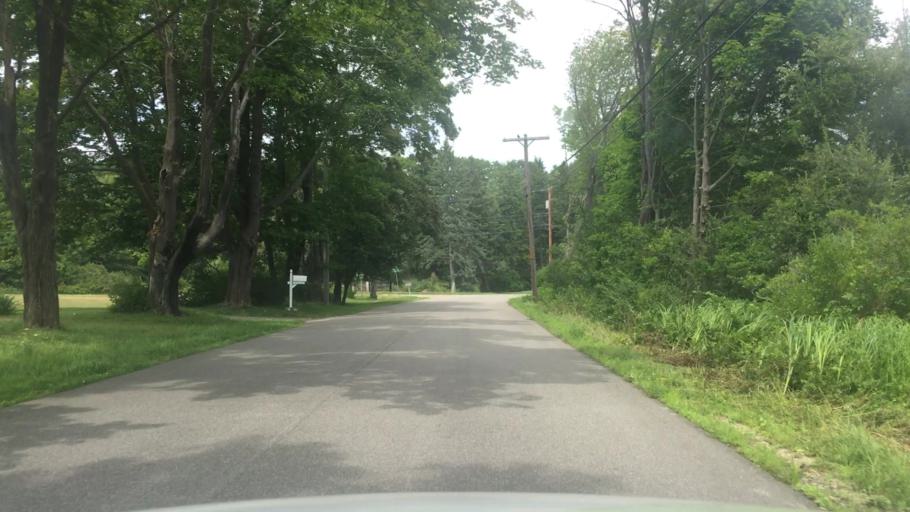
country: US
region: Maine
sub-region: Cumberland County
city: Scarborough
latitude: 43.5584
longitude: -70.2664
